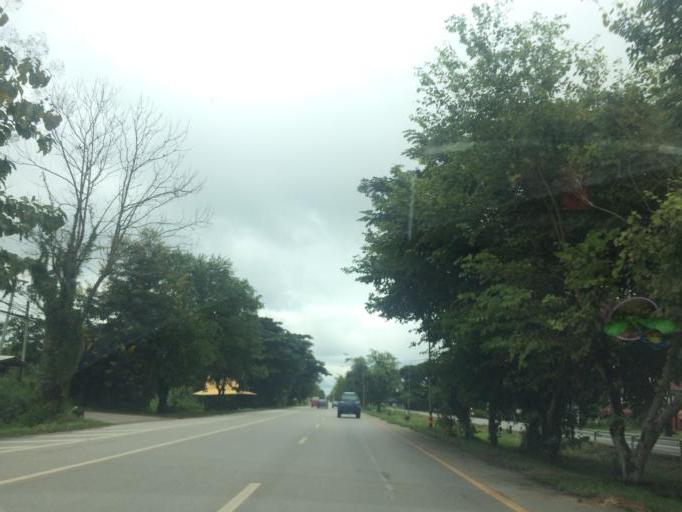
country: TH
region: Chiang Rai
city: Chiang Rai
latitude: 19.8507
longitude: 99.8103
